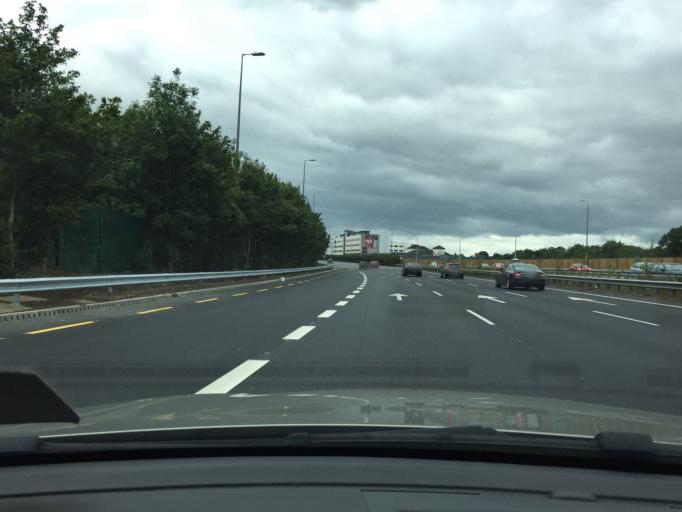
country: IE
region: Leinster
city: Clondalkin
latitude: 53.3116
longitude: -6.3977
